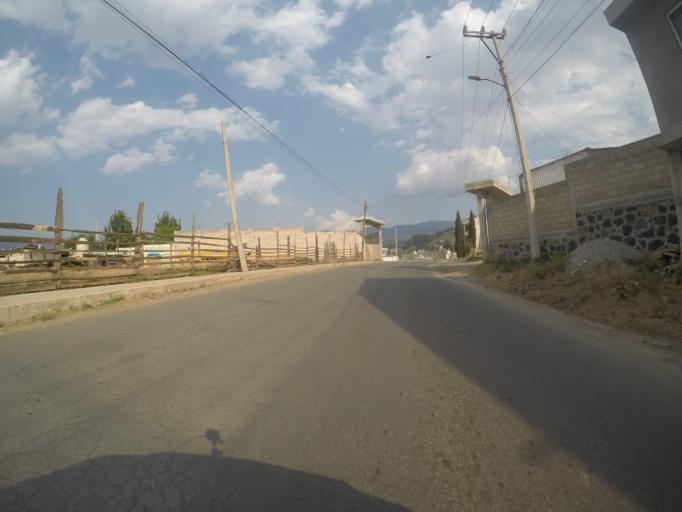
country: MX
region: Mexico
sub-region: Xalatlaco
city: Techichili
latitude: 19.1737
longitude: -99.4195
